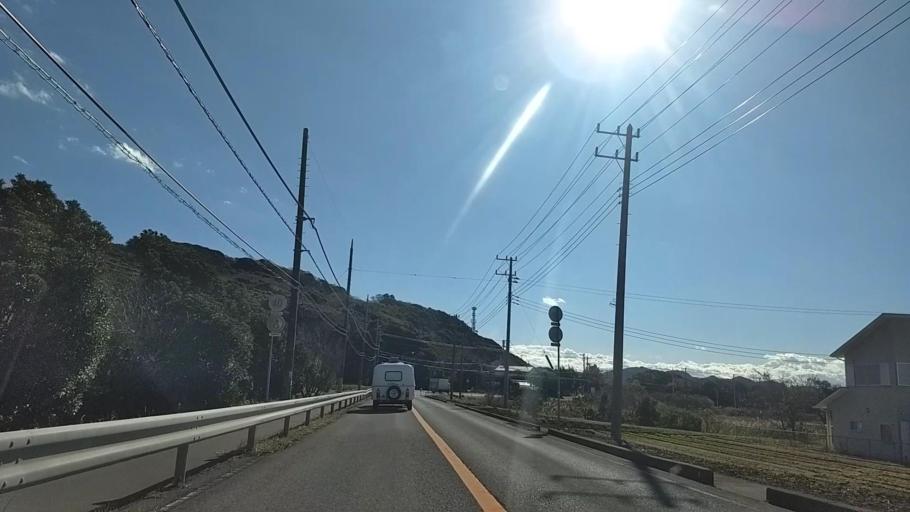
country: JP
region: Chiba
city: Tateyama
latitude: 34.9400
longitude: 139.8410
